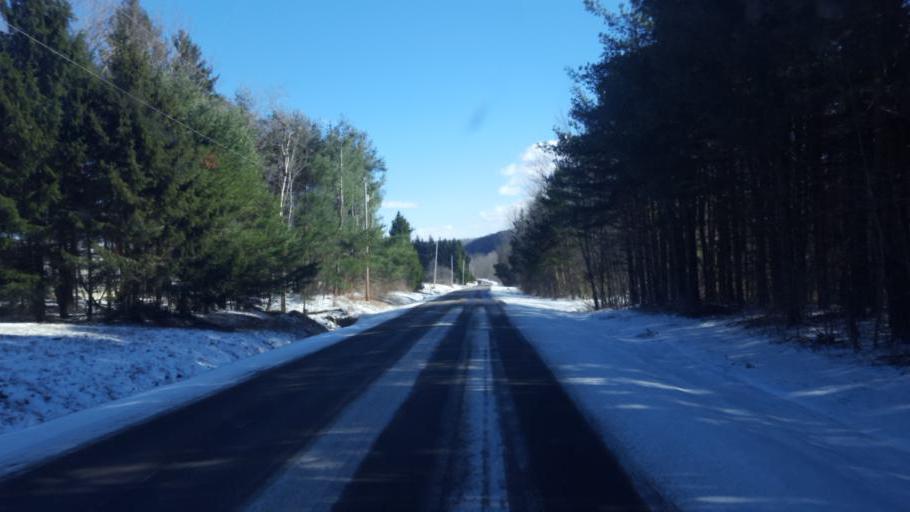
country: US
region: New York
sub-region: Allegany County
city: Belmont
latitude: 42.1782
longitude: -78.0727
